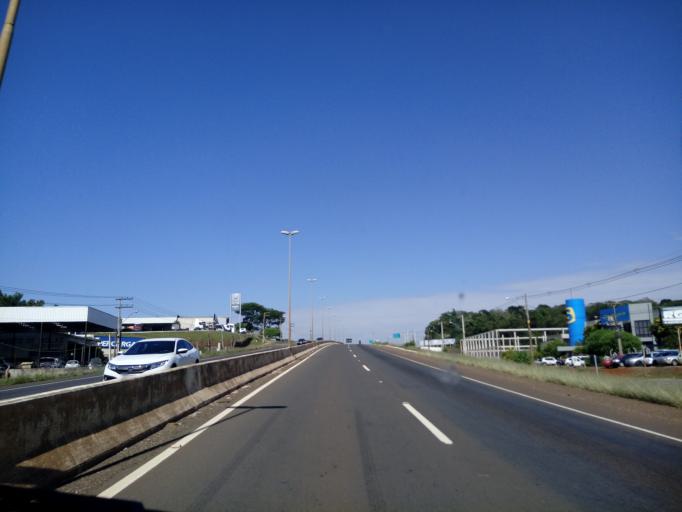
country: BR
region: Santa Catarina
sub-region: Chapeco
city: Chapeco
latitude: -27.0361
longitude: -52.6340
